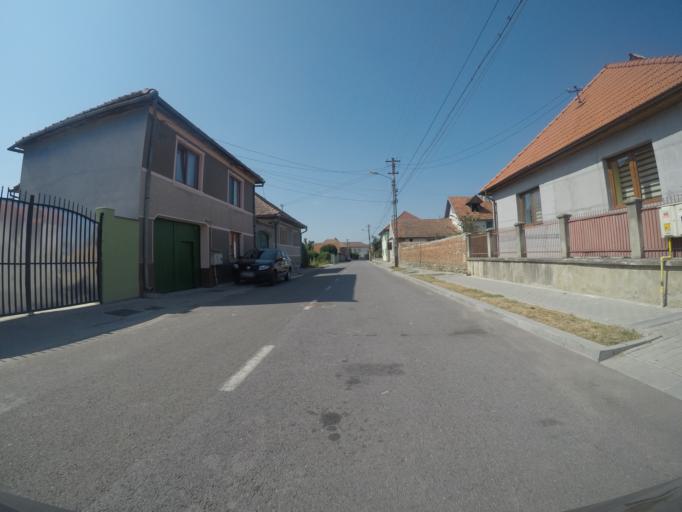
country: RO
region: Sibiu
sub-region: Comuna Avrig
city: Avrig
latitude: 45.7267
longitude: 24.3845
